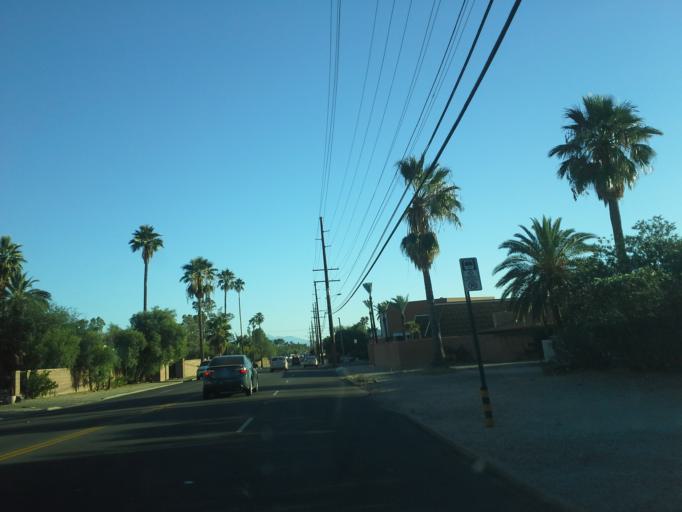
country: US
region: Arizona
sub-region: Pima County
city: Tucson
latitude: 32.2252
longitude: -110.9267
